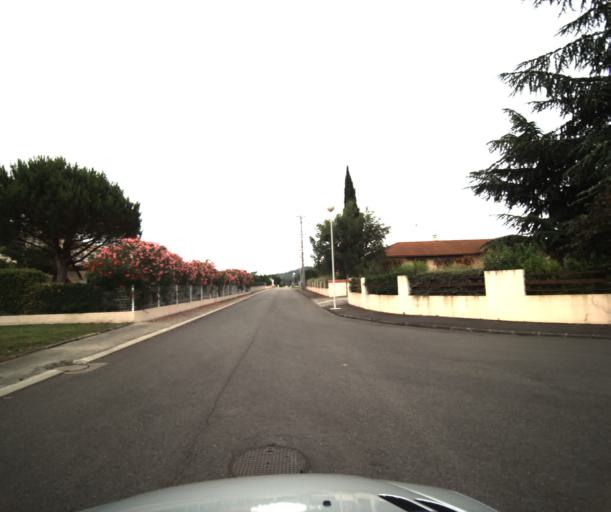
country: FR
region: Midi-Pyrenees
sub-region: Departement de la Haute-Garonne
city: Lacroix-Falgarde
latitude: 43.4926
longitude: 1.3988
